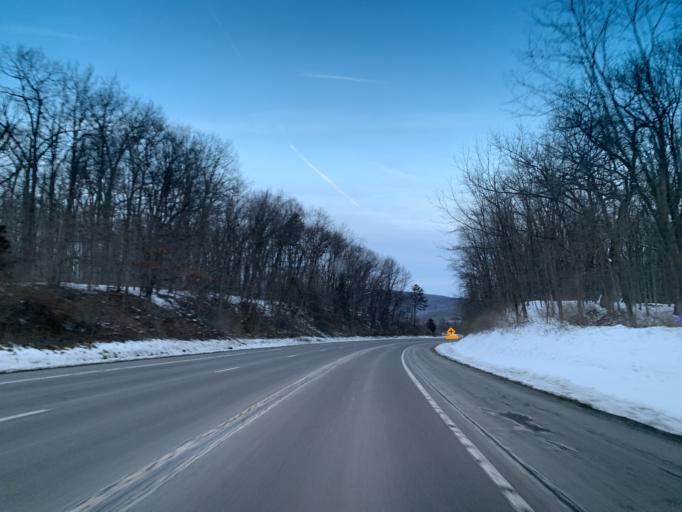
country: US
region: Maryland
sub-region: Allegany County
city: Cumberland
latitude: 39.7115
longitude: -78.6137
